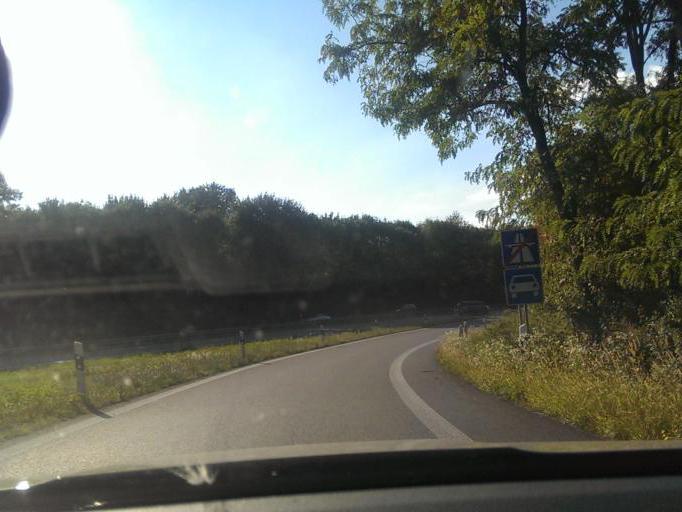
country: DE
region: Baden-Wuerttemberg
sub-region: Karlsruhe Region
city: Karlsruhe
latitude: 48.9925
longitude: 8.4331
